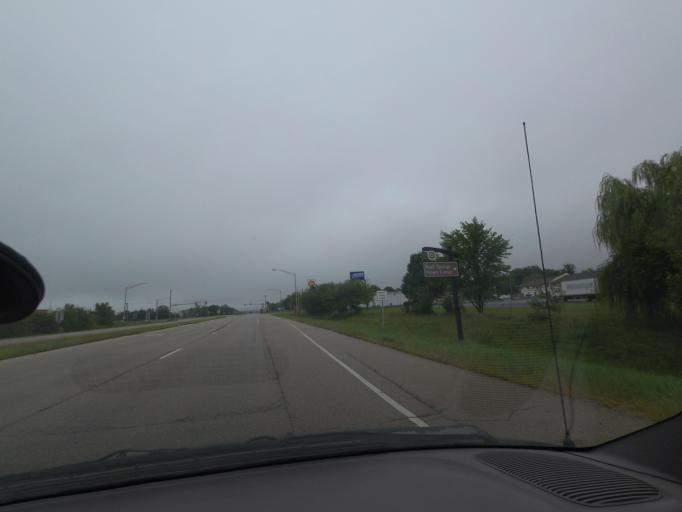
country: US
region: Illinois
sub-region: Macon County
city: Harristown
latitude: 39.8463
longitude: -89.0309
